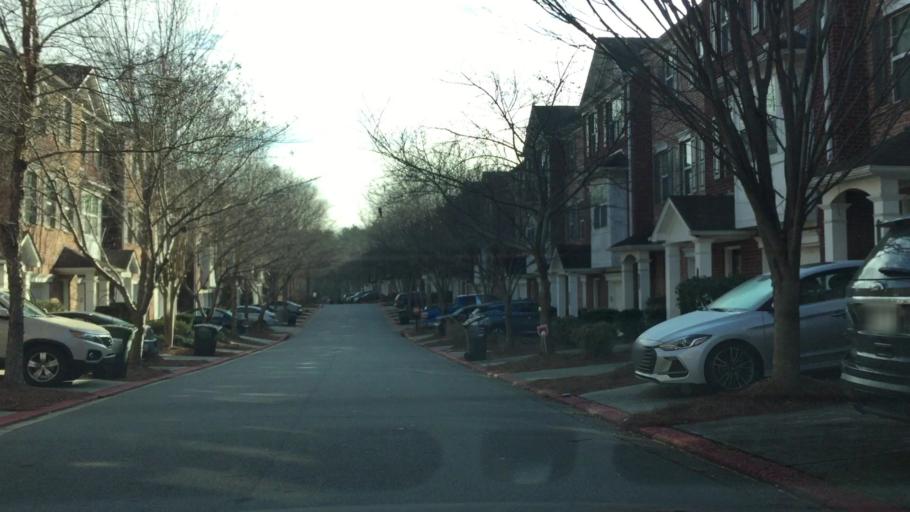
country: US
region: Georgia
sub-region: Cobb County
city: Kennesaw
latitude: 34.0088
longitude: -84.5639
